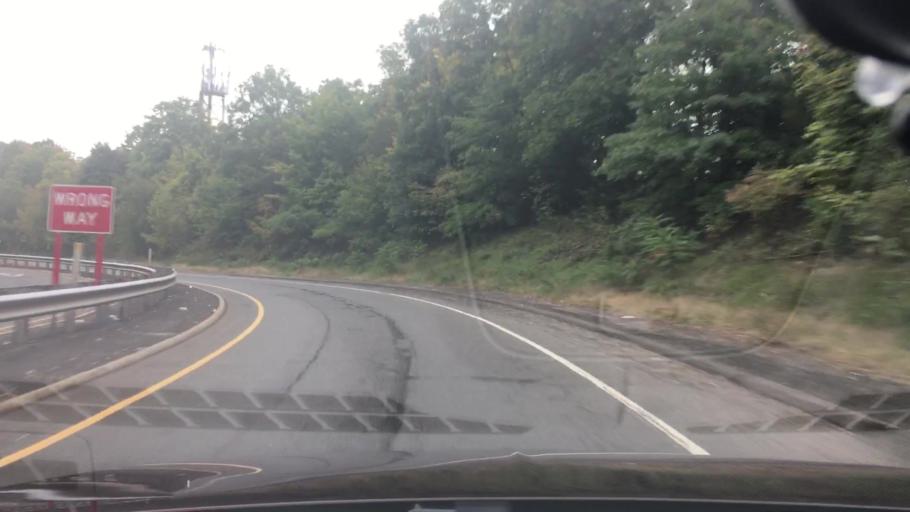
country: US
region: Connecticut
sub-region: Middlesex County
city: Cromwell
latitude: 41.6043
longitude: -72.7013
